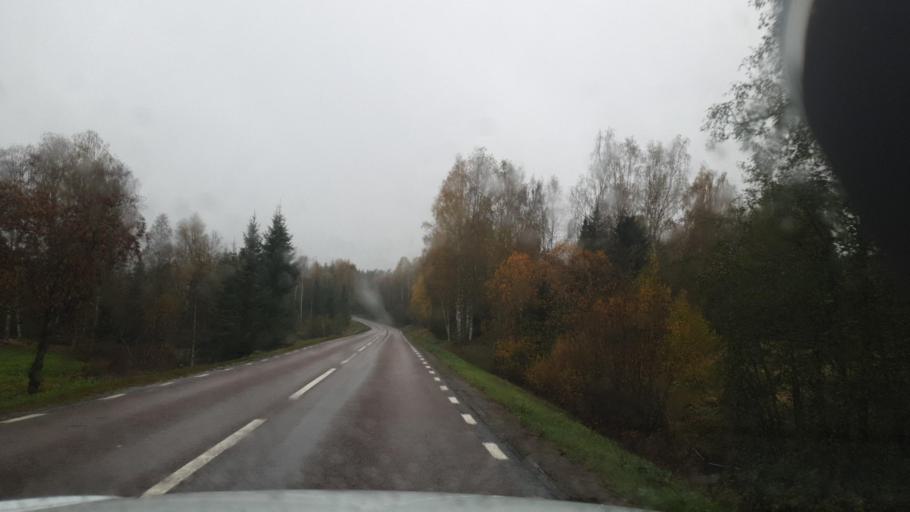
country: SE
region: Vaermland
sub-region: Eda Kommun
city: Amotfors
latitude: 59.7327
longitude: 12.2217
